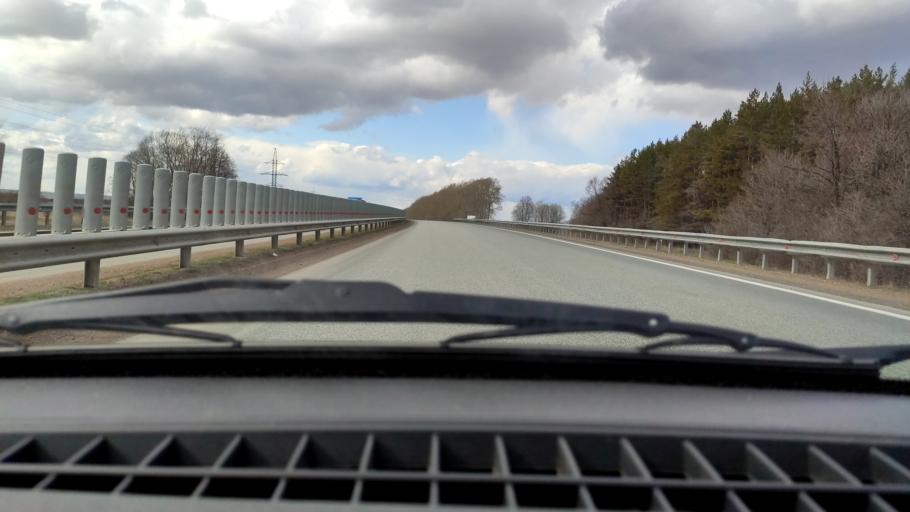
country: RU
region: Bashkortostan
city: Kushnarenkovo
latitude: 55.0468
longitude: 55.4455
